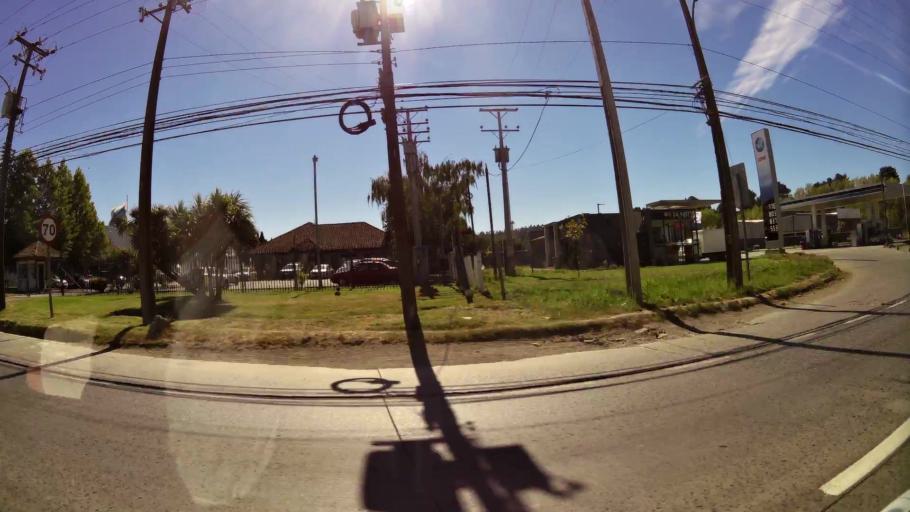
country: CL
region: Biobio
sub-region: Provincia de Concepcion
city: Penco
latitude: -36.7766
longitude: -73.0176
